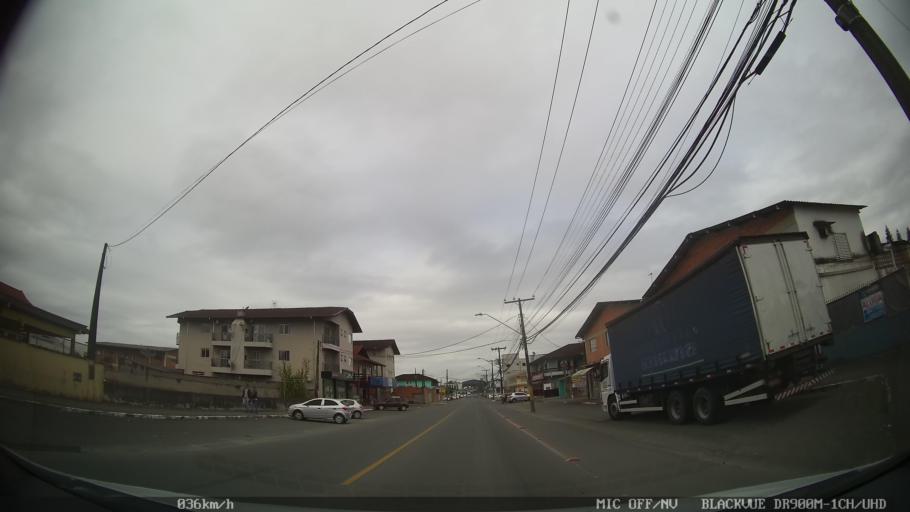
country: BR
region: Santa Catarina
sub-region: Joinville
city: Joinville
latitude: -26.2658
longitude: -48.8724
